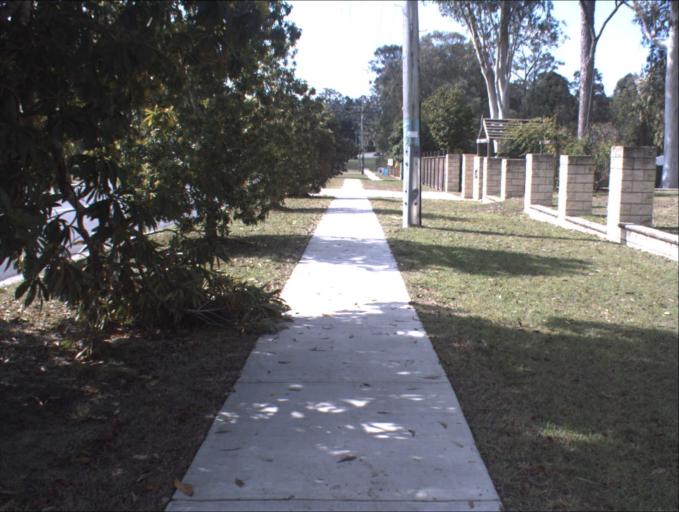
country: AU
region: Queensland
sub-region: Logan
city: Park Ridge South
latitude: -27.7014
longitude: 153.0103
